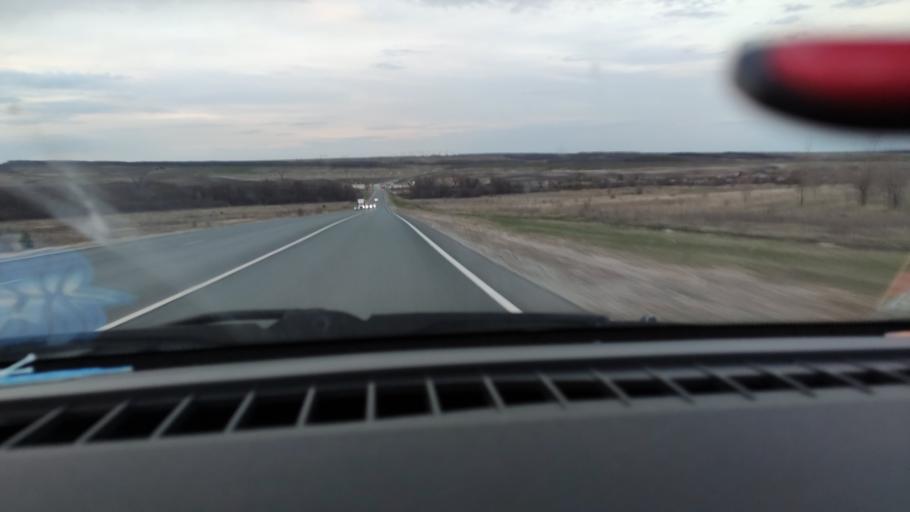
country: RU
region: Saratov
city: Sinodskoye
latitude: 51.9188
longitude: 46.5594
